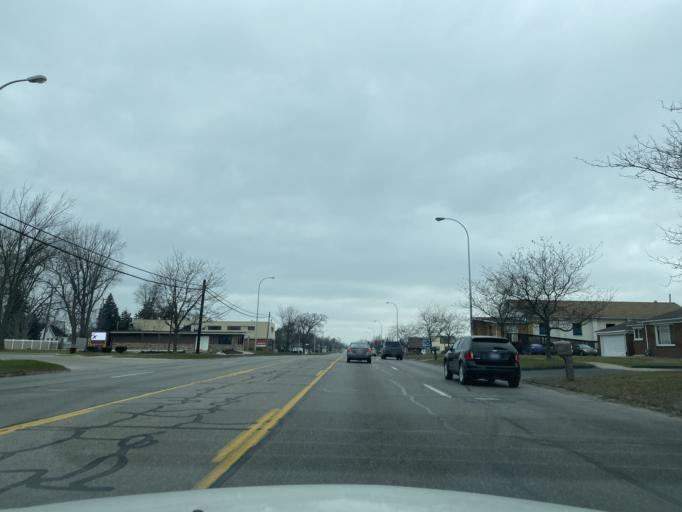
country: US
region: Michigan
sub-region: Wayne County
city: Taylor
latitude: 42.1976
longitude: -83.2702
